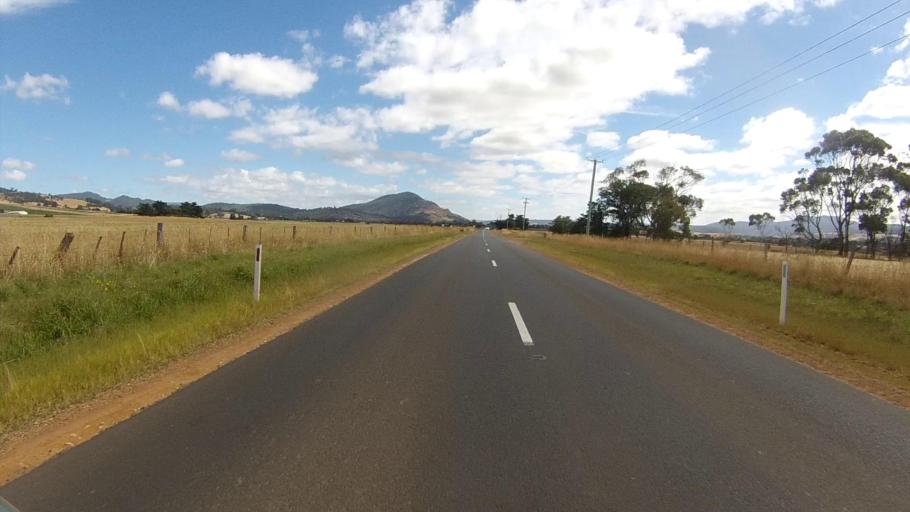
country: AU
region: Tasmania
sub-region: Clarence
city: Cambridge
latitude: -42.7047
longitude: 147.4300
